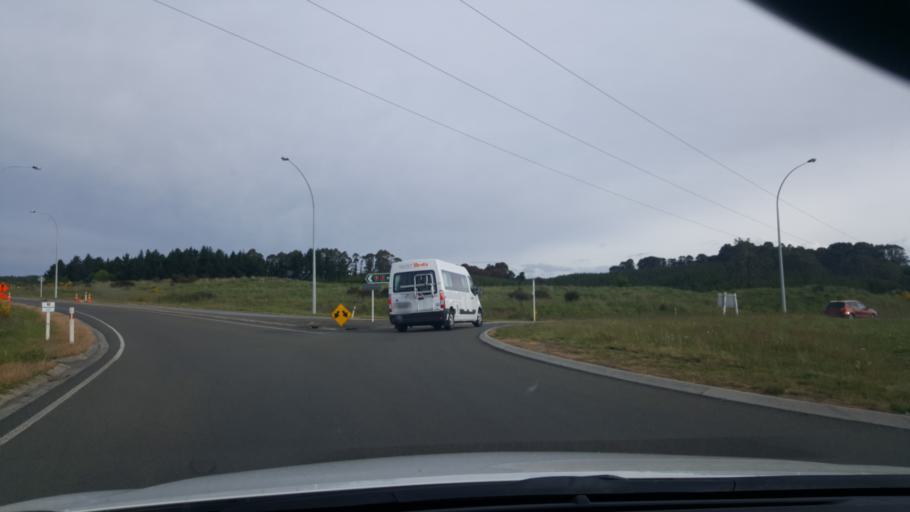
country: NZ
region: Waikato
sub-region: Taupo District
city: Taupo
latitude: -38.7041
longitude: 176.1121
